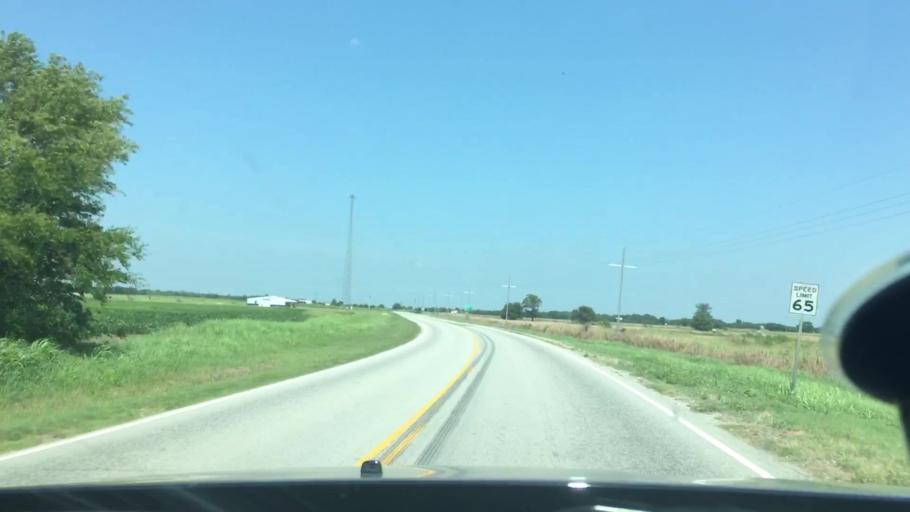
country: US
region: Oklahoma
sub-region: Coal County
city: Coalgate
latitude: 34.5007
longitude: -96.4064
